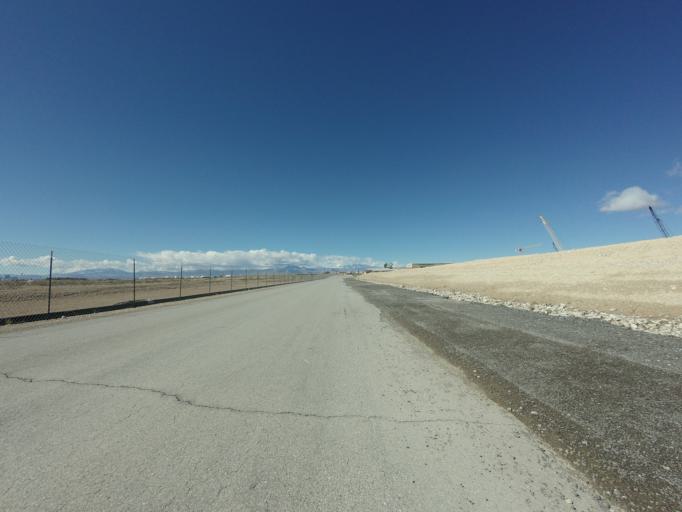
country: US
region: Nevada
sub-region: Clark County
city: Nellis Air Force Base
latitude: 36.2585
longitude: -115.0298
